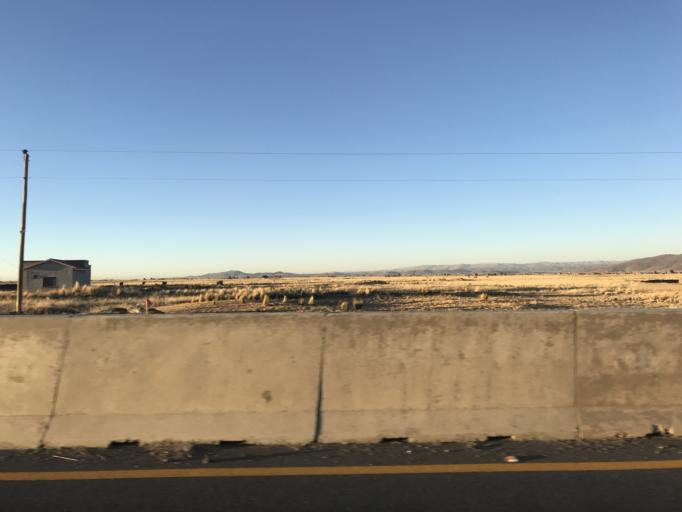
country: BO
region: La Paz
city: Batallas
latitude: -16.2989
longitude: -68.5028
